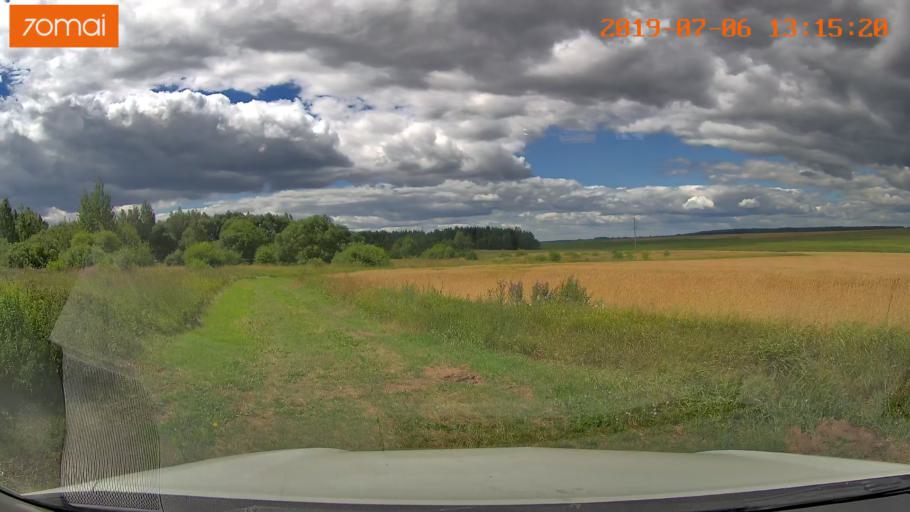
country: BY
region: Minsk
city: Enyerhyetykaw
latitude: 53.6609
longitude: 27.0042
